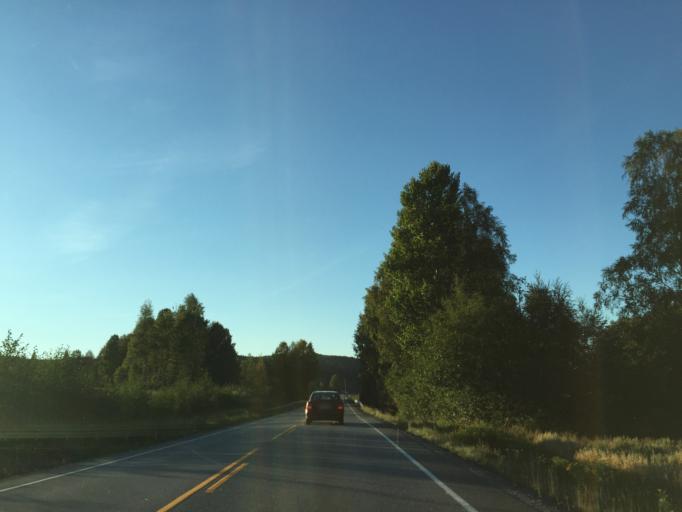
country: NO
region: Hedmark
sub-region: Nord-Odal
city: Sand
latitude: 60.3725
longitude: 11.5526
